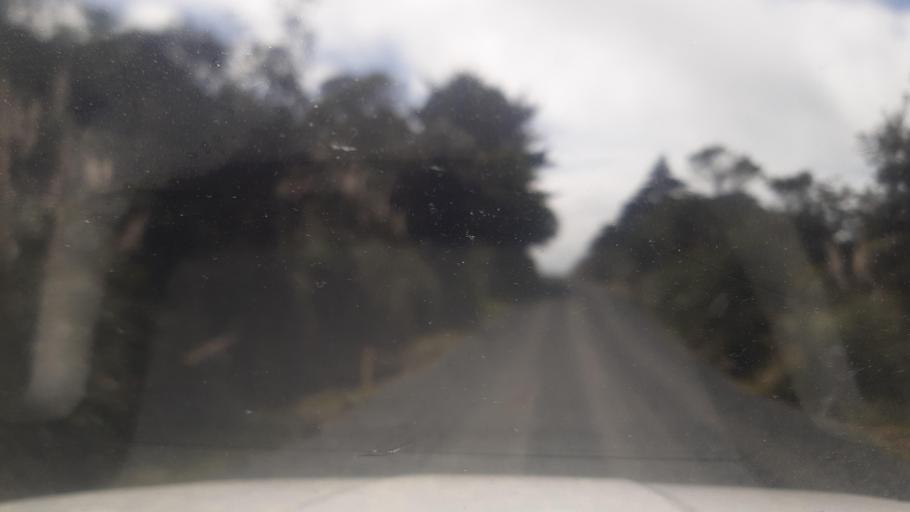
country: NZ
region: Northland
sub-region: Far North District
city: Kaitaia
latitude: -34.7416
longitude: 173.1135
